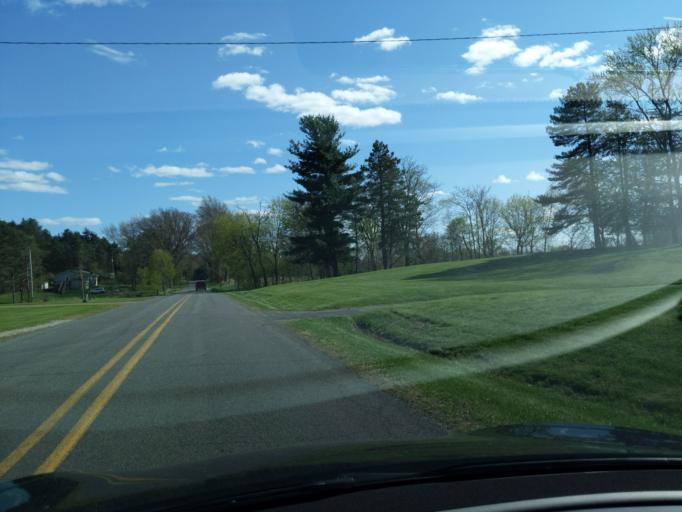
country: US
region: Michigan
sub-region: Jackson County
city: Spring Arbor
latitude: 42.3411
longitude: -84.5220
